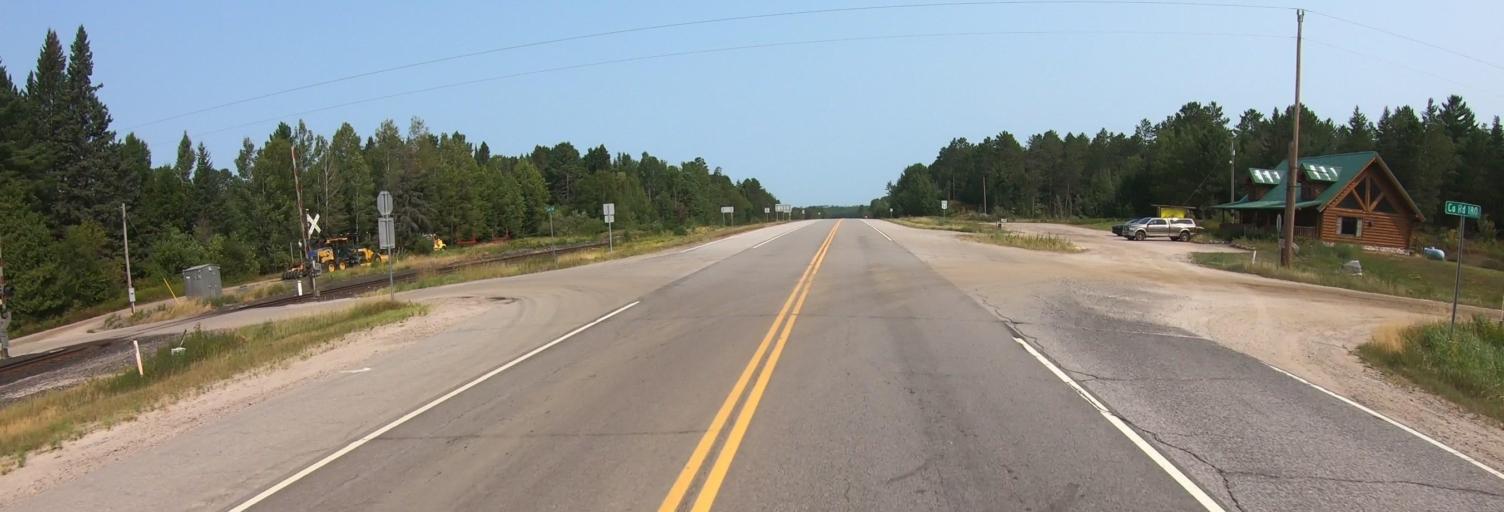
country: US
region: Minnesota
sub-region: Saint Louis County
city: Mountain Iron
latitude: 48.1016
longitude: -92.8435
